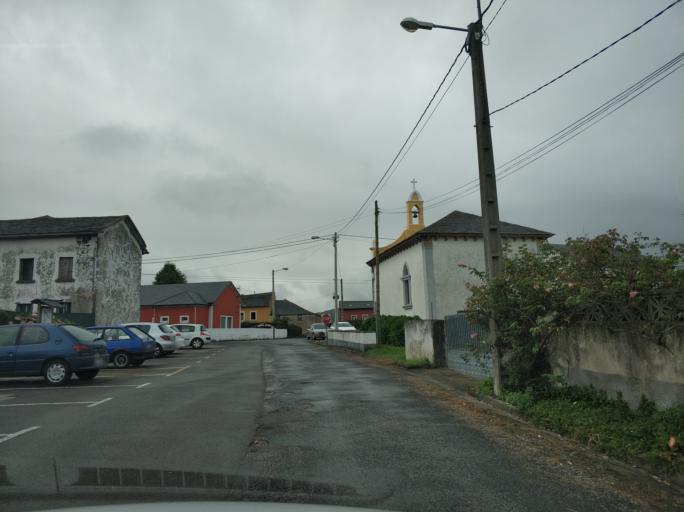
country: ES
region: Asturias
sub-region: Province of Asturias
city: Tineo
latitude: 43.5572
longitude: -6.4639
